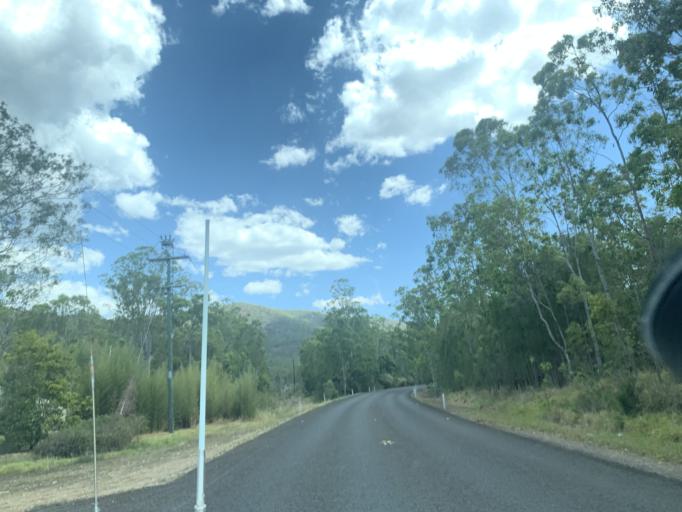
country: AU
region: Queensland
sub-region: Tablelands
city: Atherton
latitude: -17.3277
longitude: 145.4384
